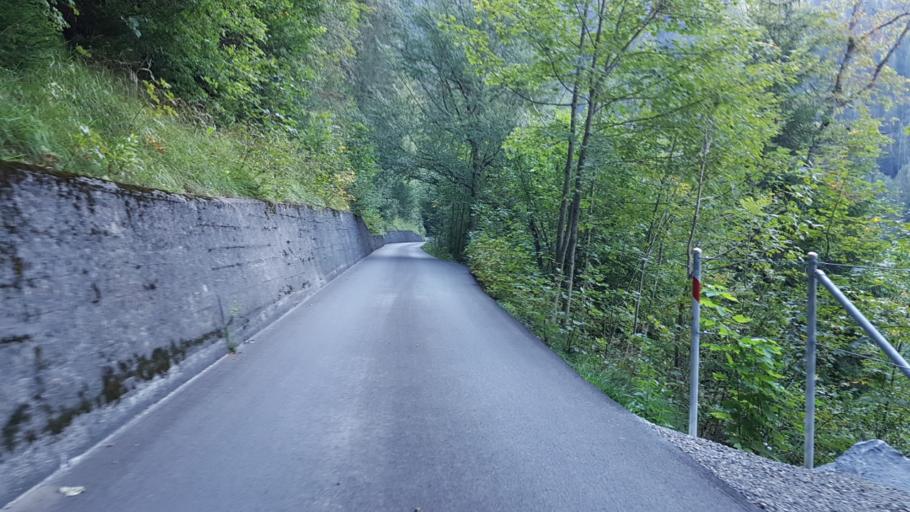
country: CH
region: Bern
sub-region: Frutigen-Niedersimmental District
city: Frutigen
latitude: 46.5517
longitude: 7.6732
